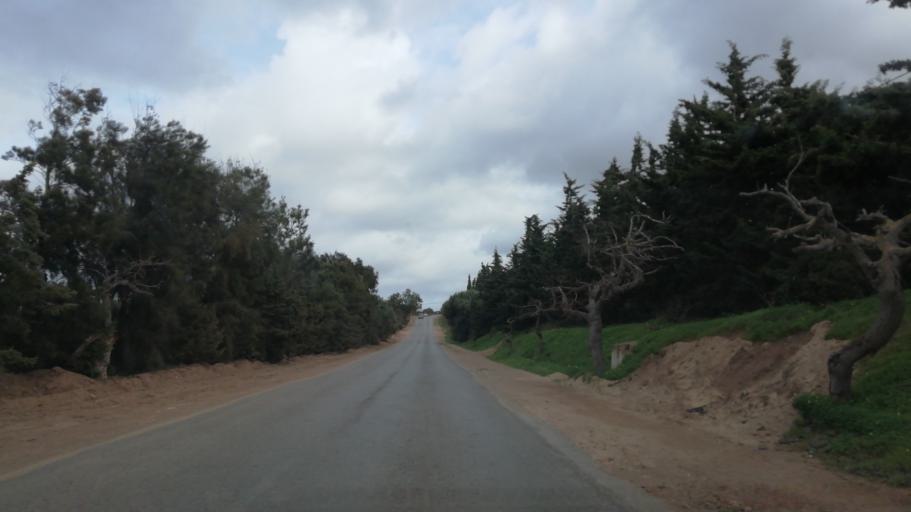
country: DZ
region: Oran
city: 'Ain el Turk
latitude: 35.7016
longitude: -0.8444
